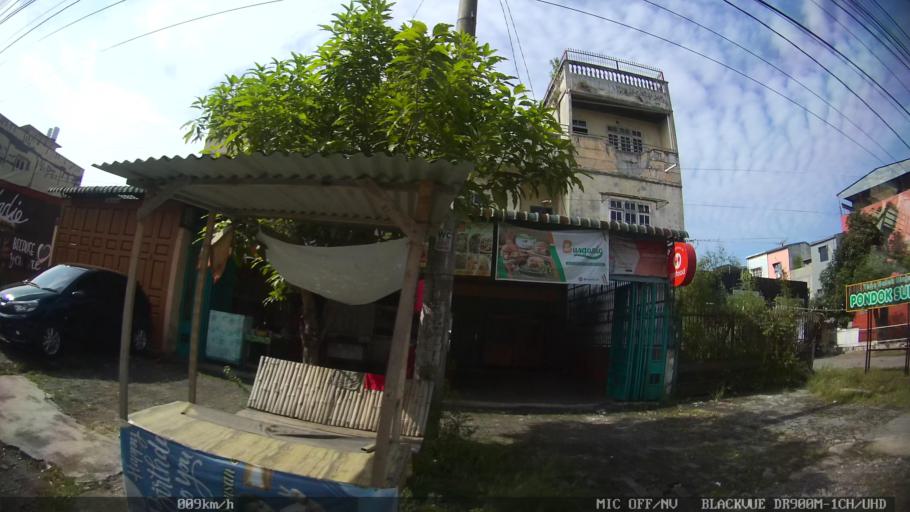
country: ID
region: North Sumatra
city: Medan
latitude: 3.6041
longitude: 98.6535
